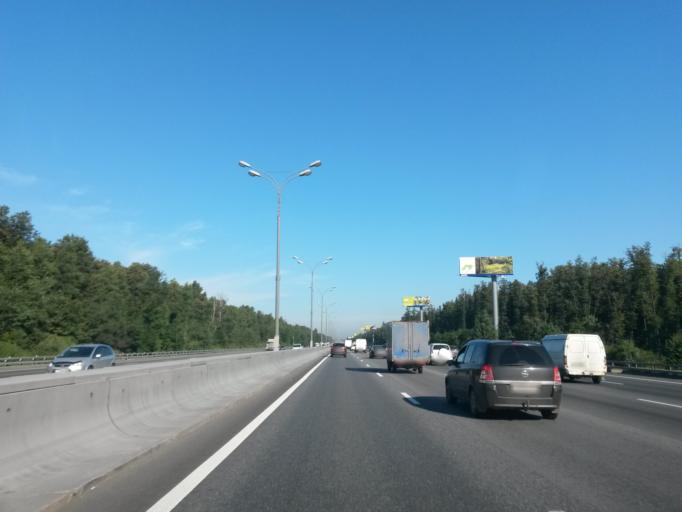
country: RU
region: Moscow
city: Gol'yanovo
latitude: 55.8403
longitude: 37.8086
